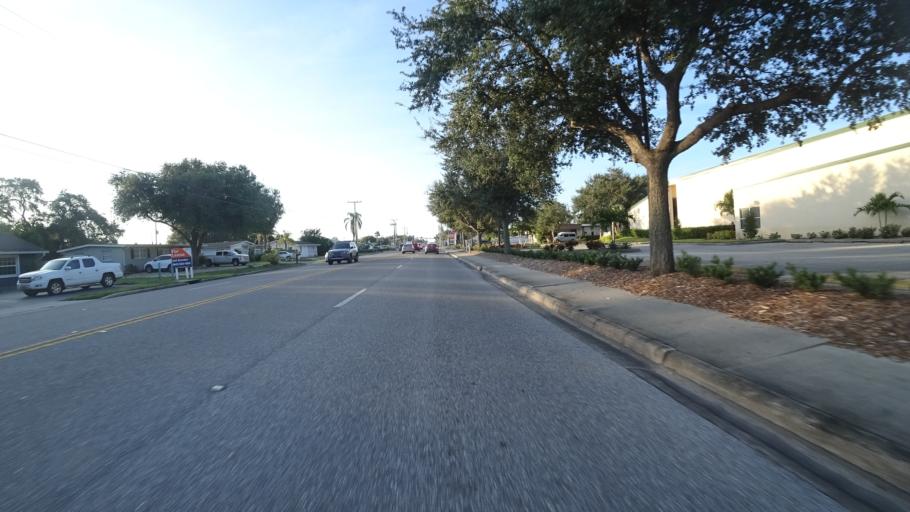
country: US
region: Florida
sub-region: Manatee County
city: South Bradenton
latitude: 27.4650
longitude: -82.5877
